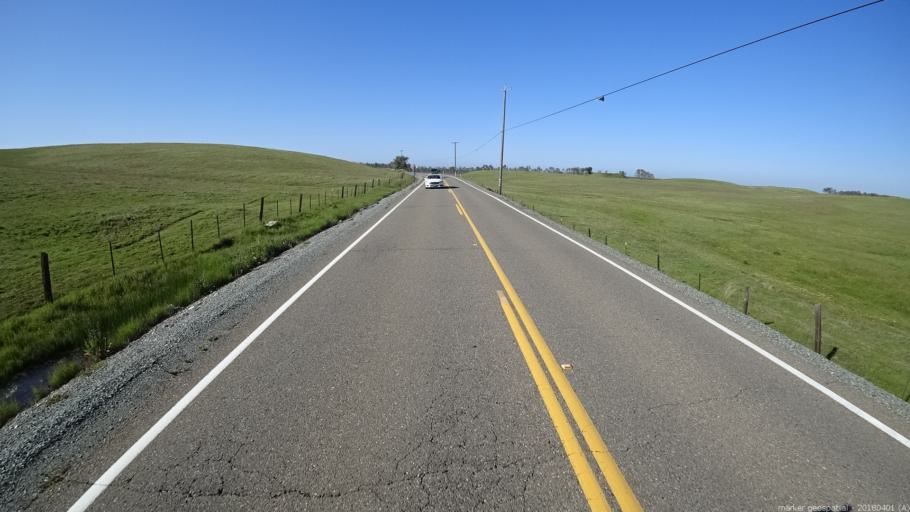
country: US
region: California
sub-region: Sacramento County
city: Rancho Murieta
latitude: 38.4458
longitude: -121.0486
